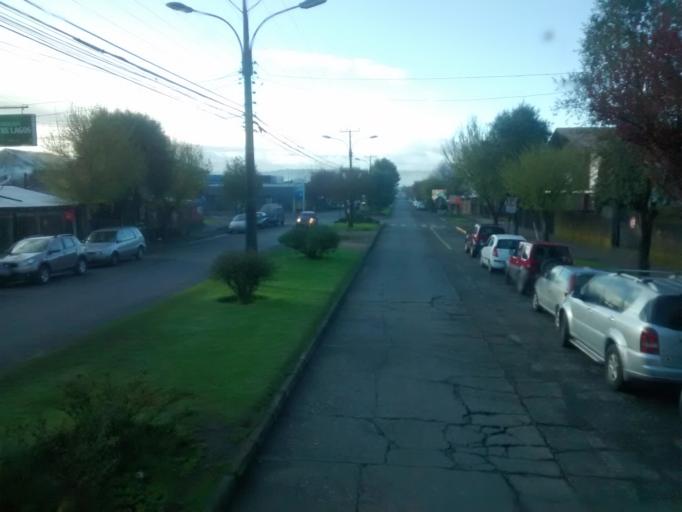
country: CL
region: Araucania
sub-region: Provincia de Cautin
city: Villarrica
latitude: -39.2795
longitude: -72.2330
